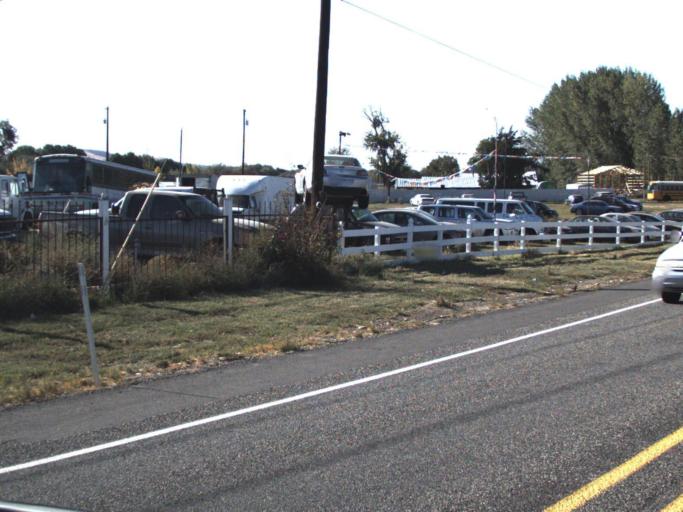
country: US
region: Washington
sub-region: Benton County
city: Finley
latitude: 46.1726
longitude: -119.0530
